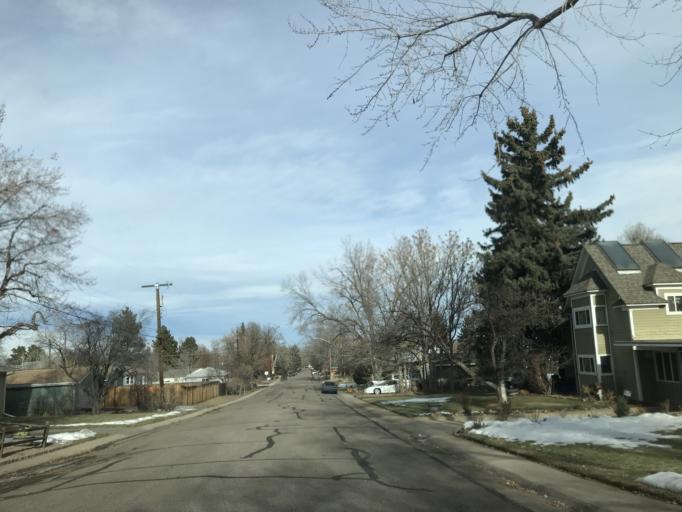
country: US
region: Colorado
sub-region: Arapahoe County
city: Littleton
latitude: 39.5977
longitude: -105.0093
